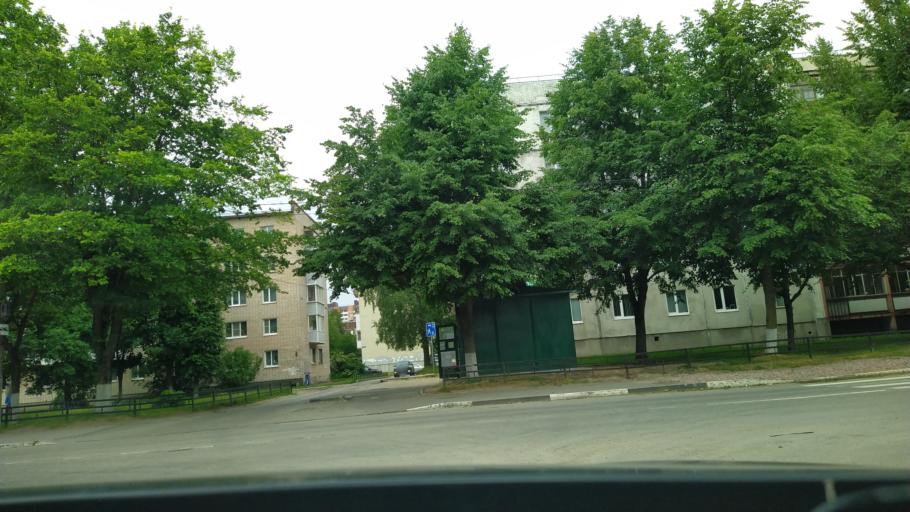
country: RU
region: Leningrad
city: Kirovsk
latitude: 59.8807
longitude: 30.9909
